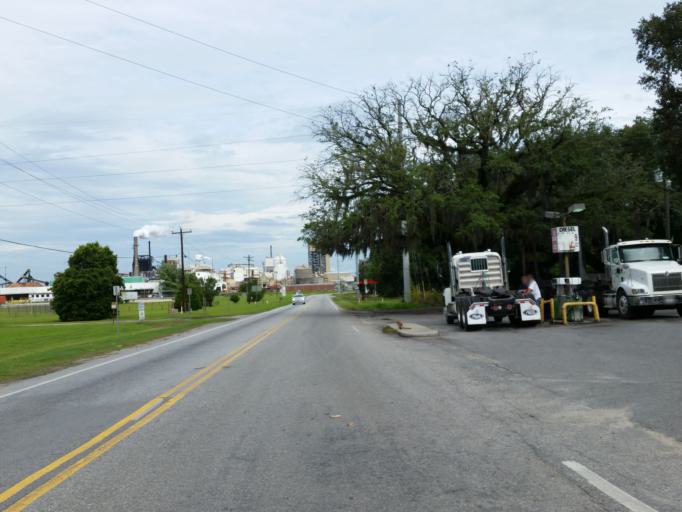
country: US
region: Georgia
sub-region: Lowndes County
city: Valdosta
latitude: 30.6969
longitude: -83.3127
